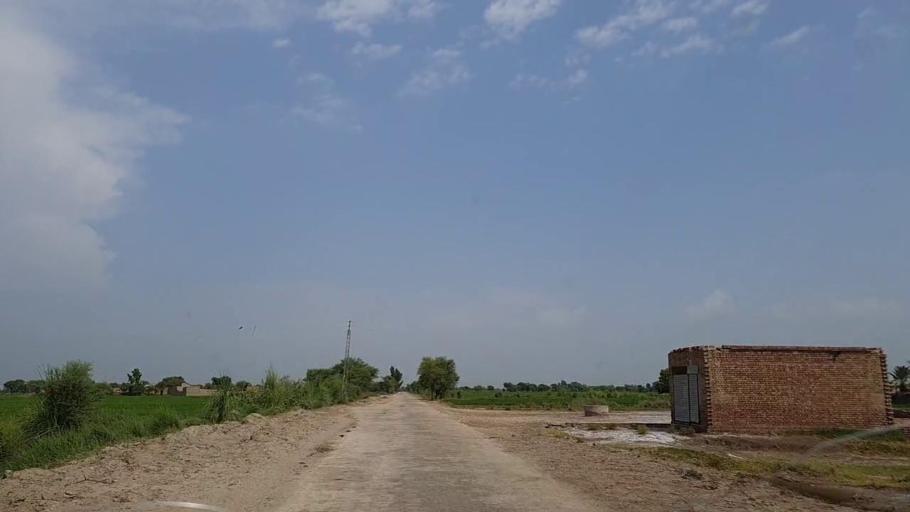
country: PK
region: Sindh
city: Khanpur
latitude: 27.8462
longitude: 69.4576
